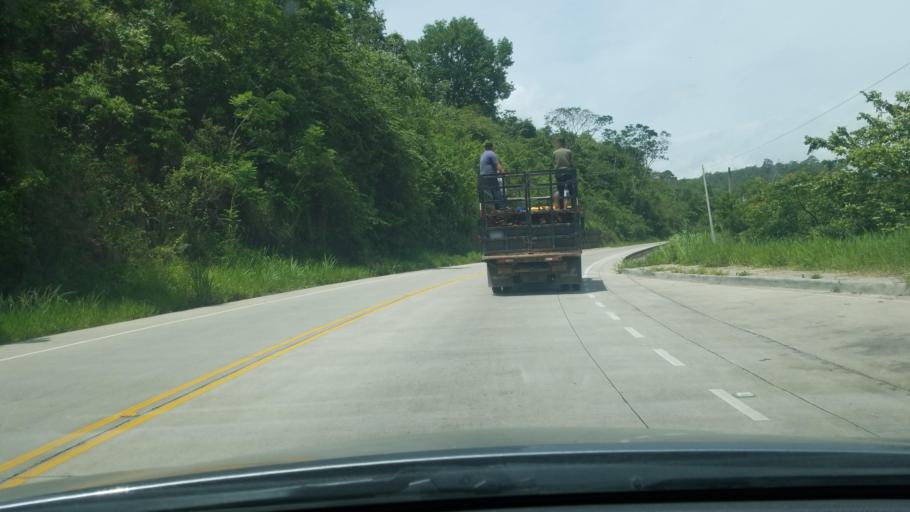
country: HN
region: Copan
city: Agua Caliente
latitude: 14.8647
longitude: -88.7873
